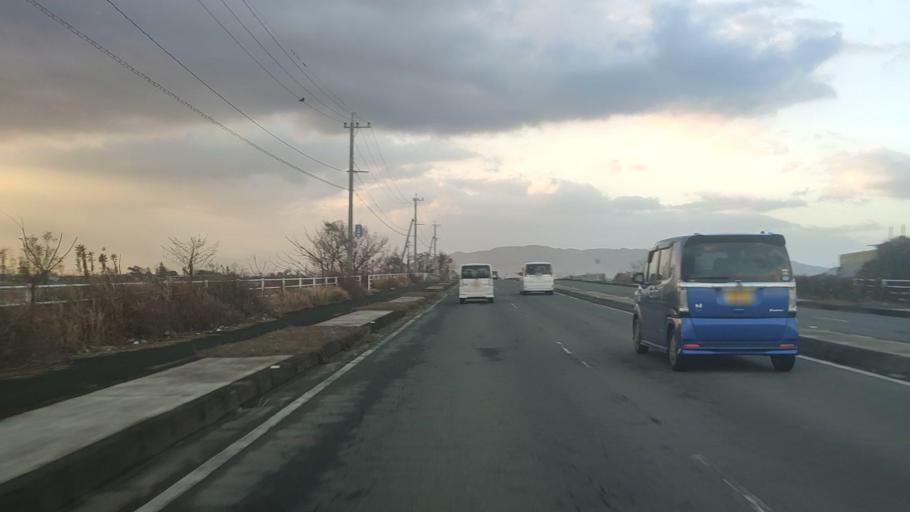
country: JP
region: Kumamoto
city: Kumamoto
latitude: 32.7543
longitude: 130.7064
